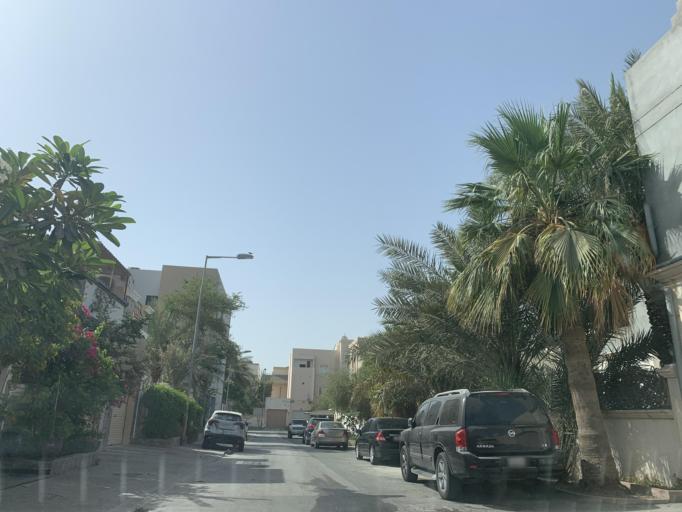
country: BH
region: Northern
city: Ar Rifa'
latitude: 26.1480
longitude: 50.5809
